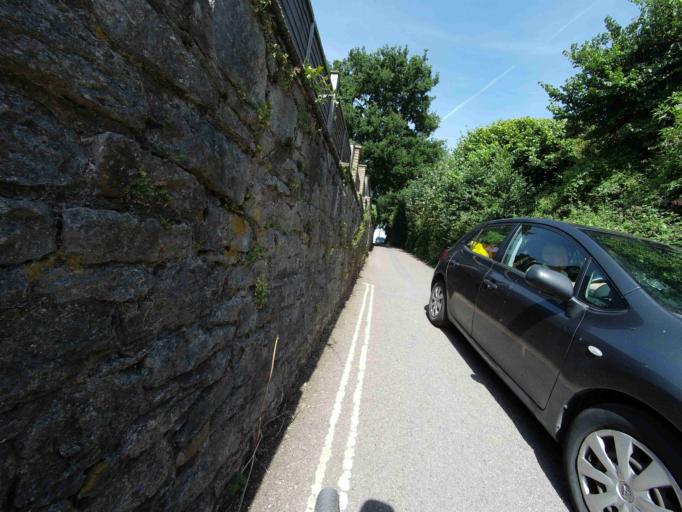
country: GB
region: England
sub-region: Devon
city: Topsham
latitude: 50.6860
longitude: -3.4708
